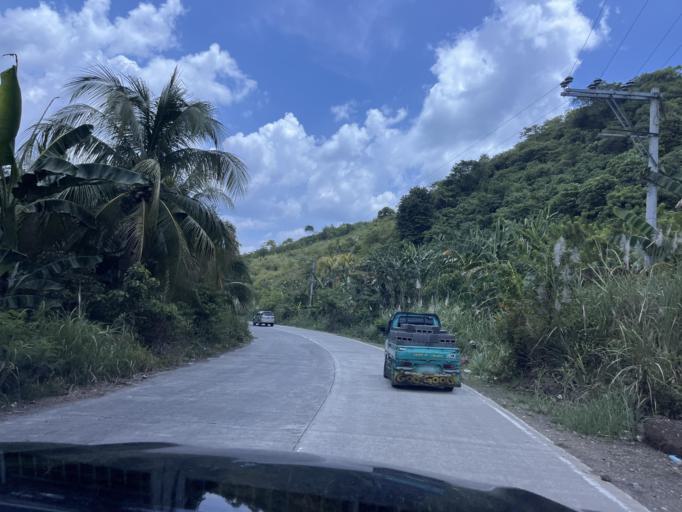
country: PH
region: Davao
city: Lacson
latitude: 7.2300
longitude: 125.4499
